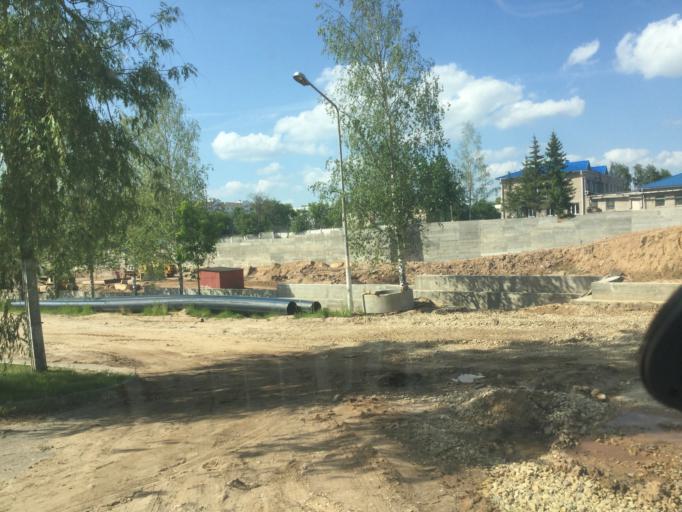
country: BY
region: Vitebsk
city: Vitebsk
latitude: 55.1673
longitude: 30.2445
